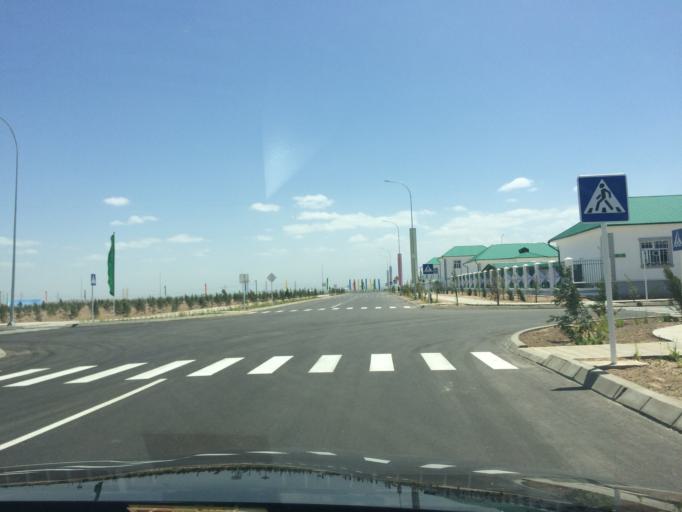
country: TM
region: Ahal
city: Abadan
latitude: 38.0951
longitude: 58.2901
